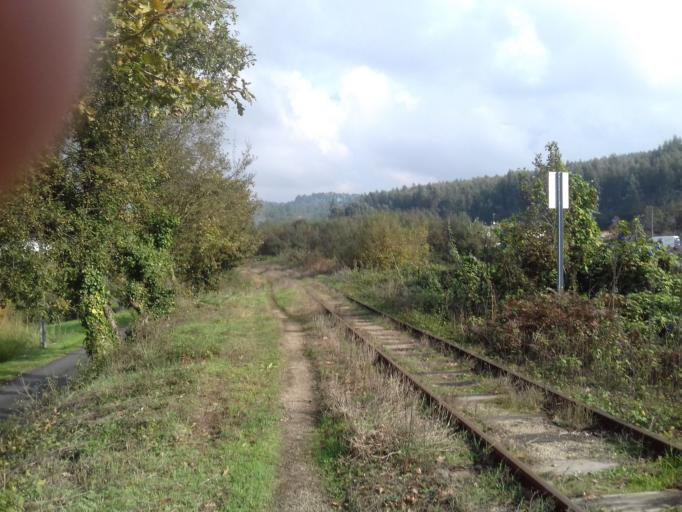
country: PT
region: Aveiro
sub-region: Albergaria-A-Velha
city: Branca
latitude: 40.7786
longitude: -8.4850
